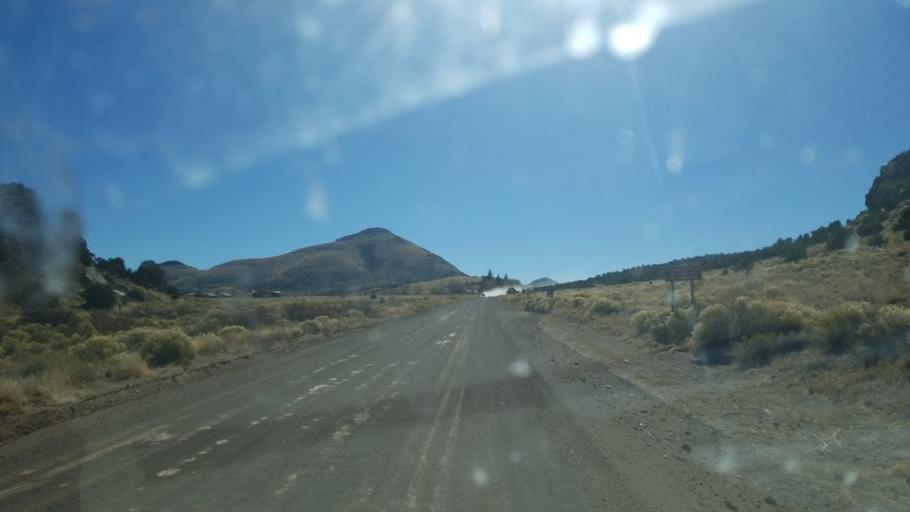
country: US
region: Colorado
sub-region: Rio Grande County
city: Del Norte
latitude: 37.6329
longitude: -106.3646
